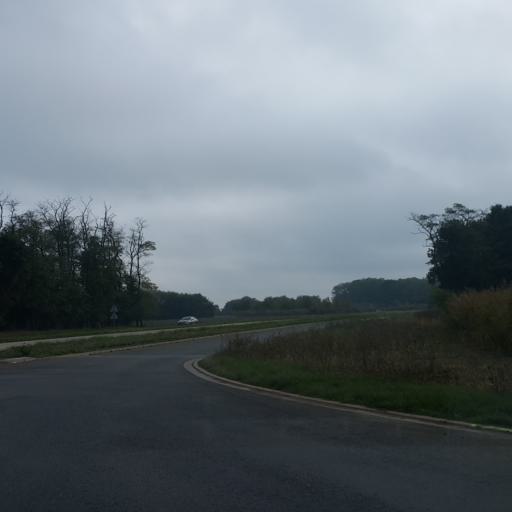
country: FR
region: Ile-de-France
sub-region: Departement de l'Essonne
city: Saint-Pierre-du-Perray
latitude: 48.6132
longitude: 2.5201
